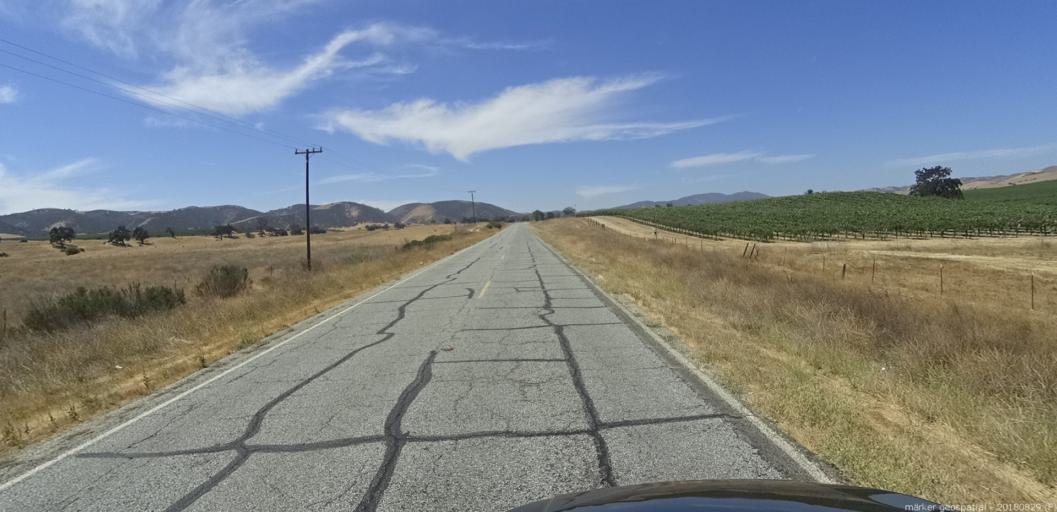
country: US
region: California
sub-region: San Luis Obispo County
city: Lake Nacimiento
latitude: 35.8731
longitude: -120.8738
